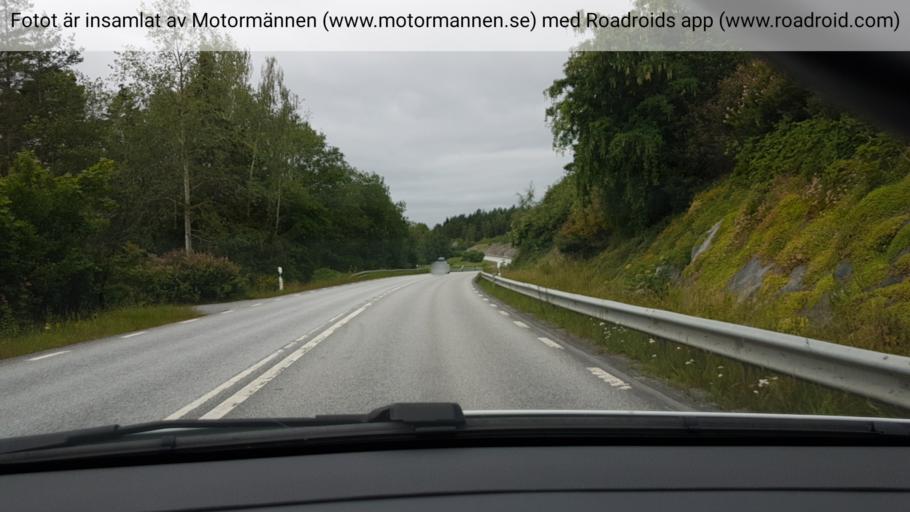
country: SE
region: Stockholm
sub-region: Vaxholms Kommun
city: Resaro
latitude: 59.4190
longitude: 18.3026
